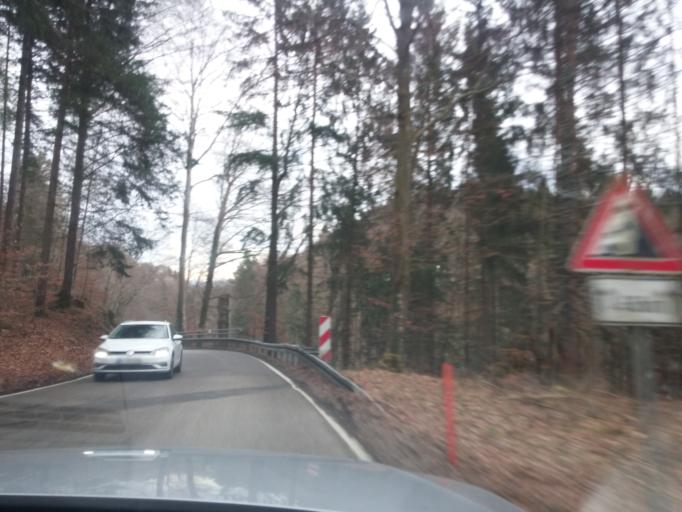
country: DE
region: Bavaria
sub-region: Upper Bavaria
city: Moosach
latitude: 48.0400
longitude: 11.8594
